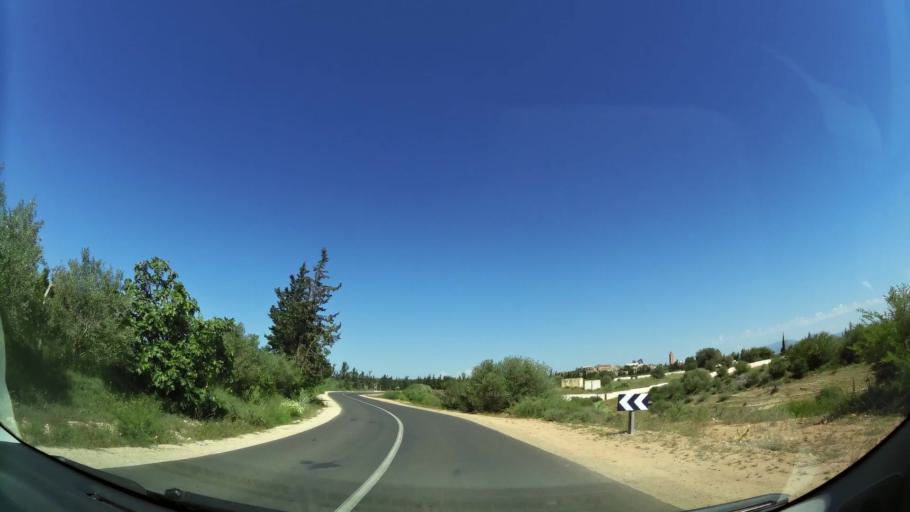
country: MA
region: Oriental
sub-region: Berkane-Taourirt
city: Madagh
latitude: 35.0396
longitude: -2.4247
